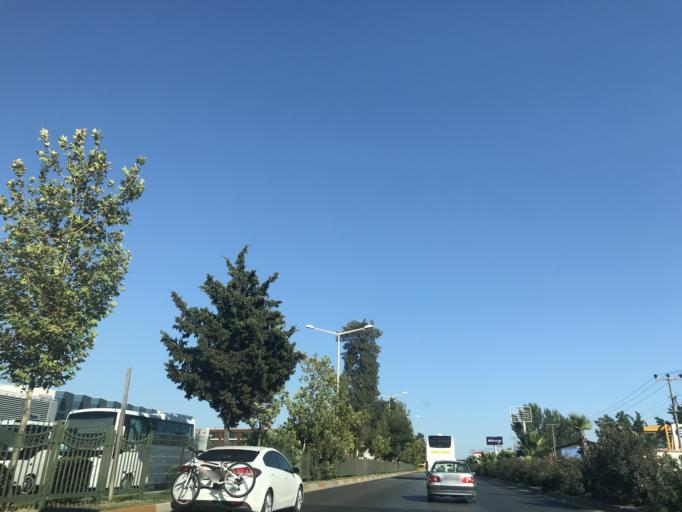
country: TR
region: Antalya
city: Antalya
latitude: 36.9057
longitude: 30.7517
